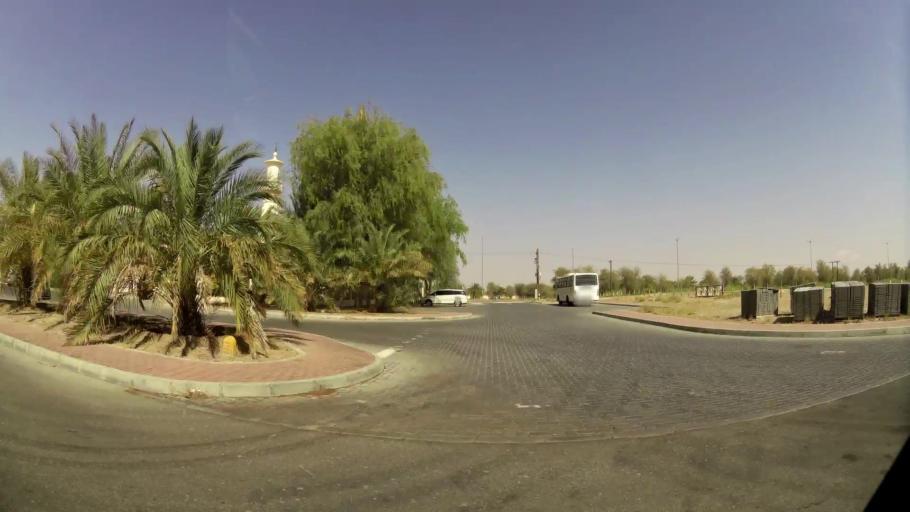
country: OM
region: Al Buraimi
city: Al Buraymi
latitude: 24.3063
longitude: 55.7950
